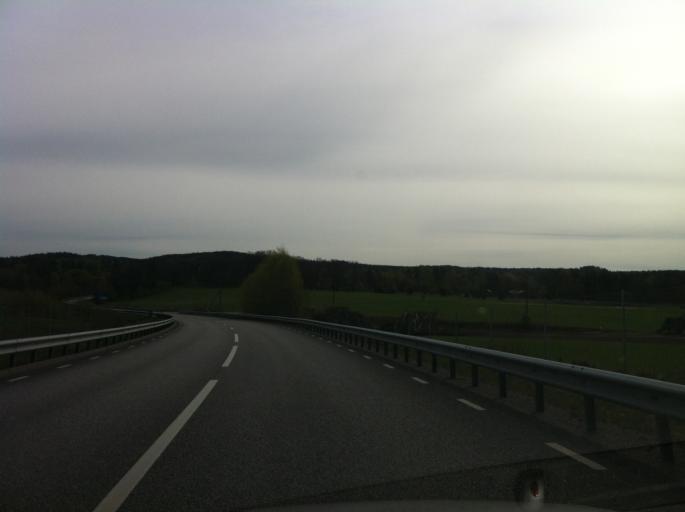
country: SE
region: Vaestra Goetaland
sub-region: Marks Kommun
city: Kinna
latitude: 57.4813
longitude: 12.6850
